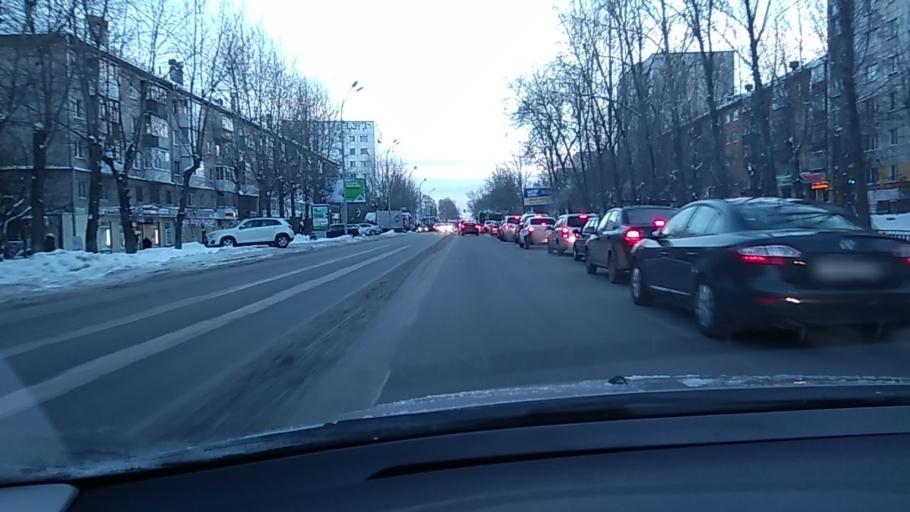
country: RU
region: Sverdlovsk
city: Yekaterinburg
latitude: 56.8283
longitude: 60.6370
